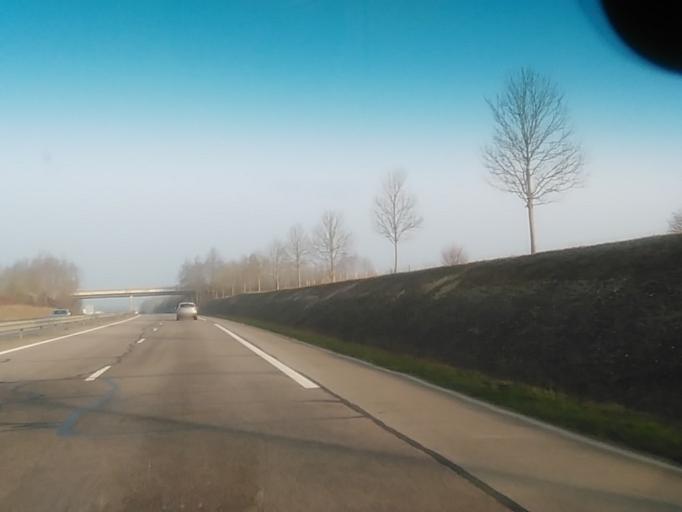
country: FR
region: Lower Normandy
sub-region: Departement du Calvados
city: Potigny
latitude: 48.9443
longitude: -0.2132
